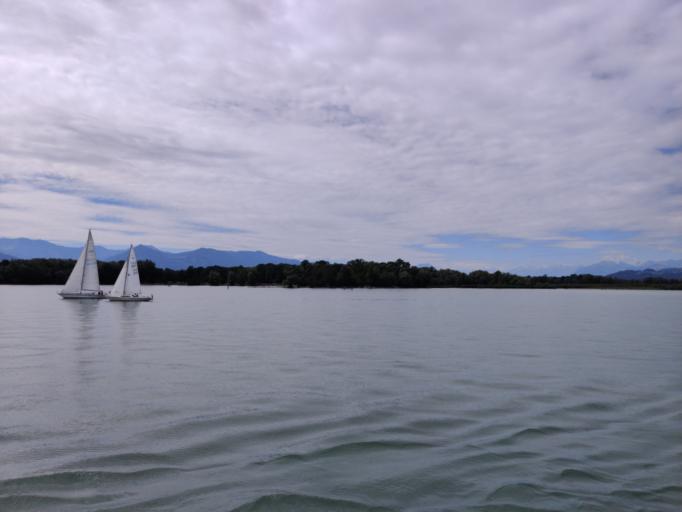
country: AT
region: Vorarlberg
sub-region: Politischer Bezirk Bregenz
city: Hard
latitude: 47.5108
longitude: 9.7004
